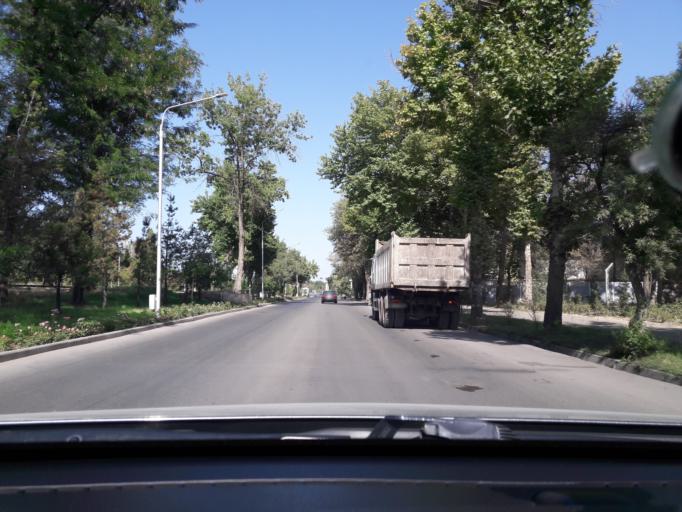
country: TJ
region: Dushanbe
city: Dushanbe
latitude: 38.5686
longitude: 68.7506
